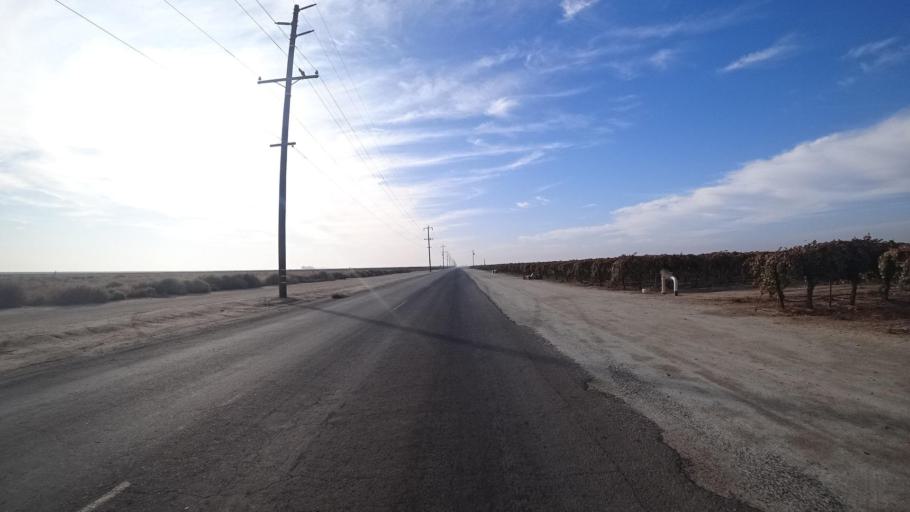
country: US
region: California
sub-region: Kern County
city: Delano
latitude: 35.7420
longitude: -119.2054
